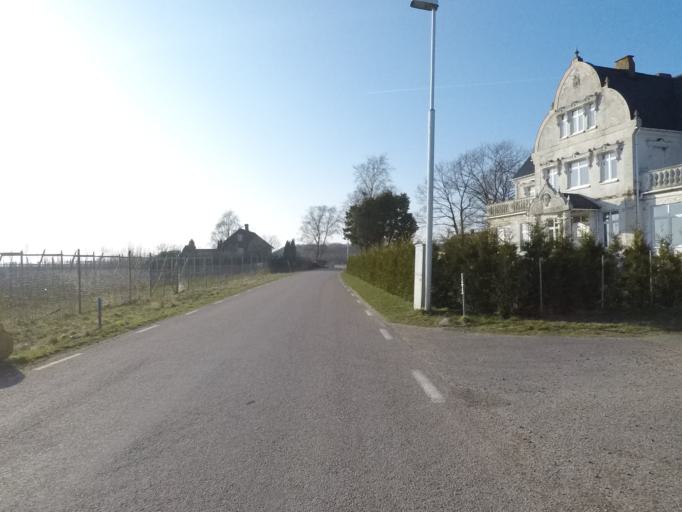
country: SE
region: Skane
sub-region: Hoganas Kommun
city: Hoganas
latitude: 56.2473
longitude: 12.6379
